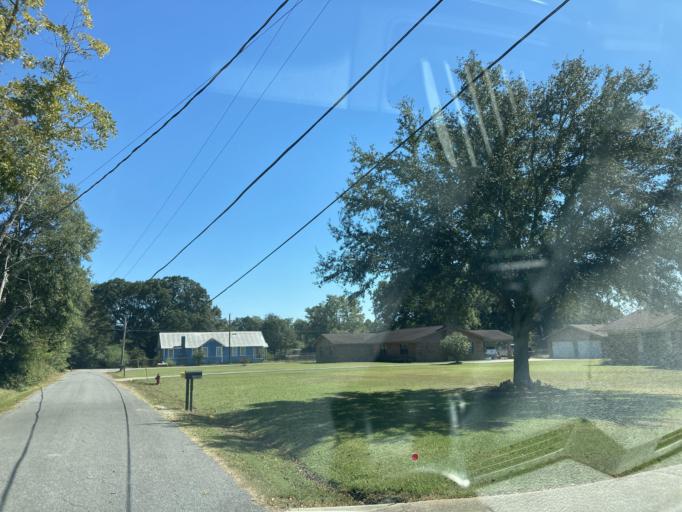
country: US
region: Mississippi
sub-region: Jackson County
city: Saint Martin
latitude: 30.4721
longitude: -88.8761
